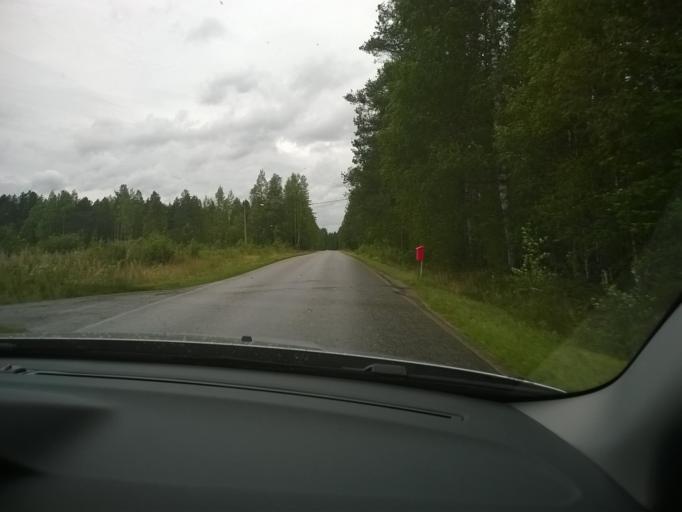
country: FI
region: Kainuu
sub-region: Kehys-Kainuu
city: Kuhmo
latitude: 64.1349
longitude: 29.4306
